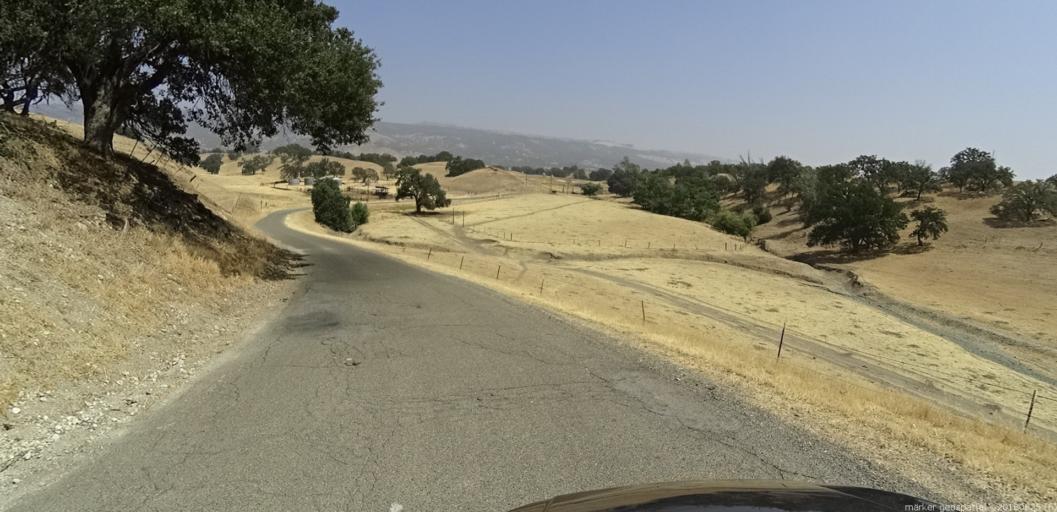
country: US
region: California
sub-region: San Luis Obispo County
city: Shandon
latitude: 35.8751
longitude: -120.3841
